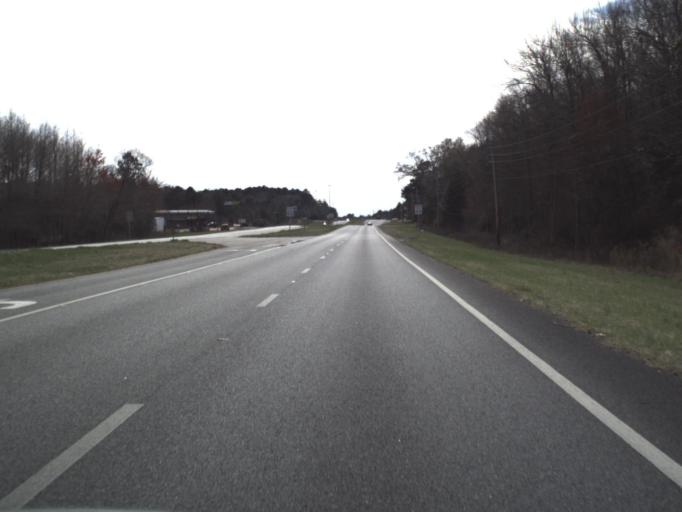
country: US
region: Florida
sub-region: Jackson County
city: Marianna
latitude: 30.7639
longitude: -85.3769
